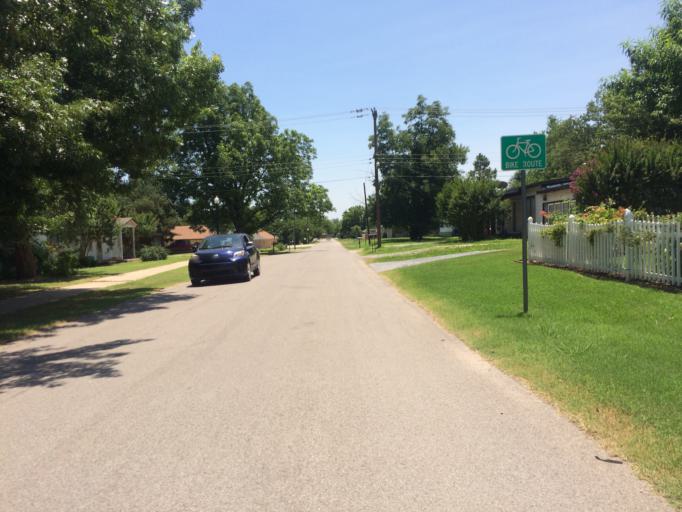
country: US
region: Oklahoma
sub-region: Cleveland County
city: Norman
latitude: 35.2213
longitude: -97.4366
